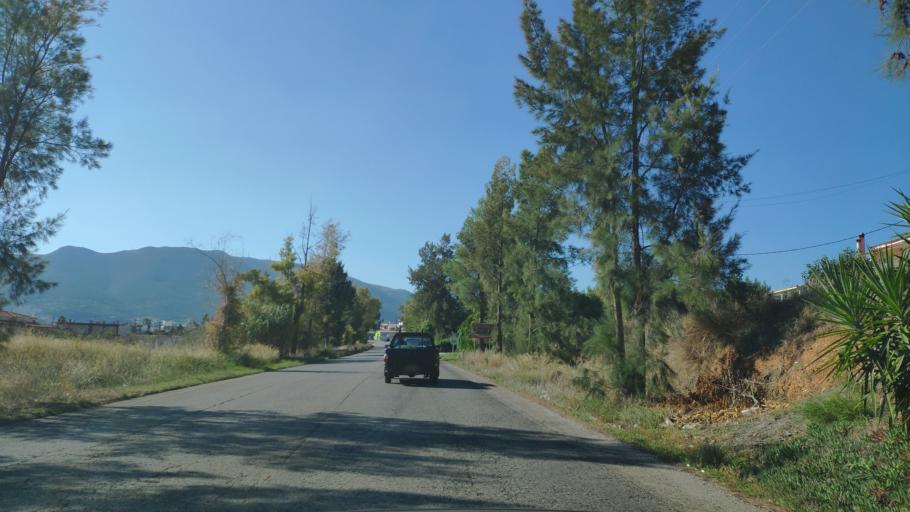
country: GR
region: Peloponnese
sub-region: Nomos Korinthias
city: Khiliomodhi
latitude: 37.8166
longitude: 22.8735
